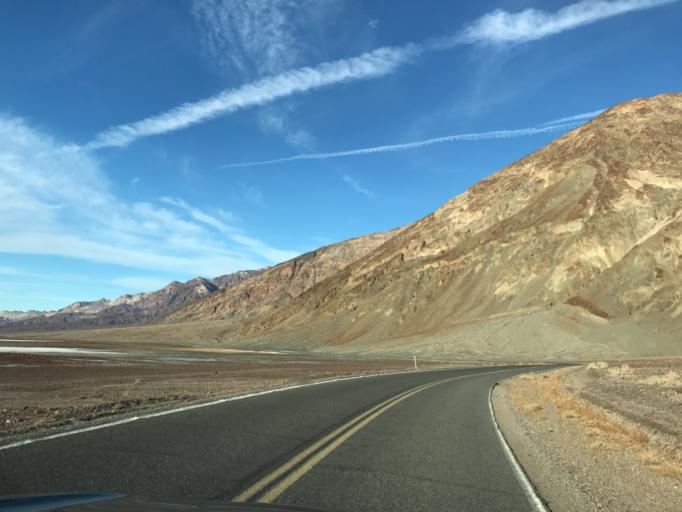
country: US
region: Nevada
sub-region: Nye County
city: Beatty
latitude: 36.2118
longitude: -116.7751
